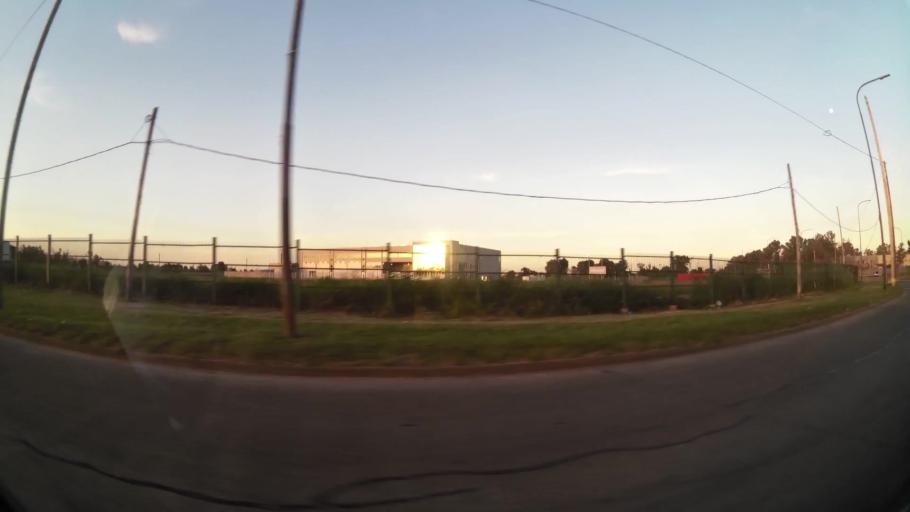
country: AR
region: Buenos Aires F.D.
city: Villa Lugano
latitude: -34.6726
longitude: -58.4591
